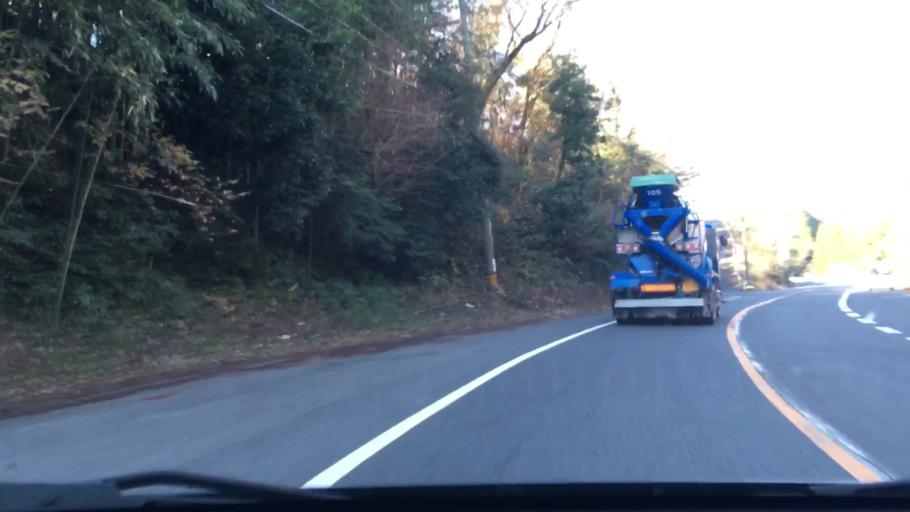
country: JP
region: Kagoshima
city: Kajiki
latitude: 31.7638
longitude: 130.6875
